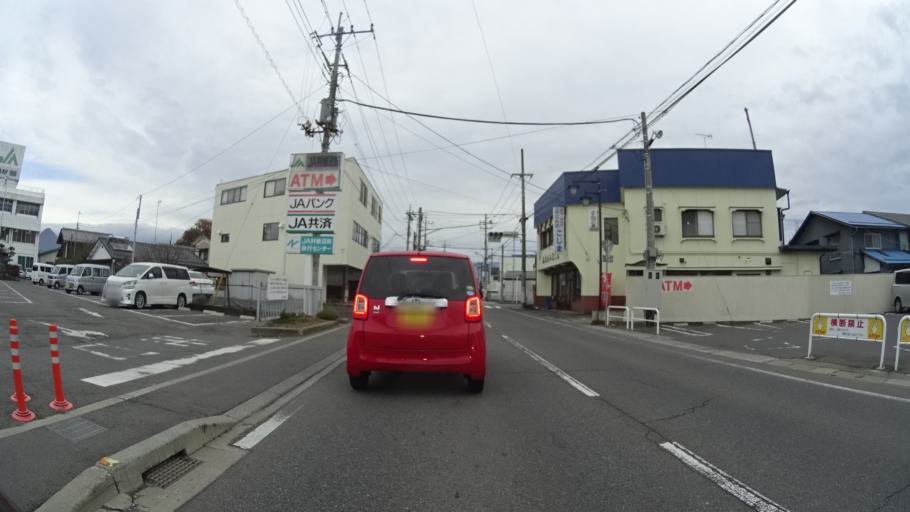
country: JP
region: Gunma
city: Numata
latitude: 36.6497
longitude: 139.0578
